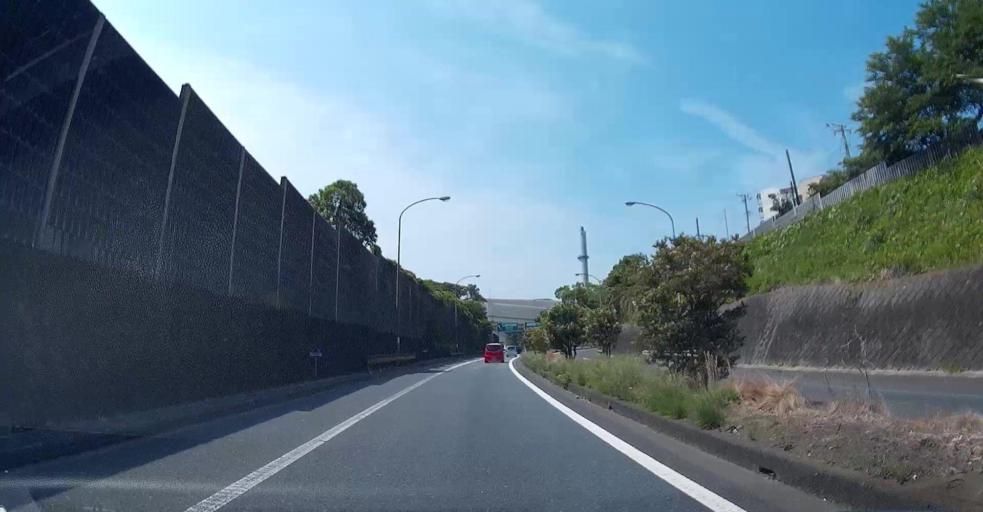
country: JP
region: Kanagawa
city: Yokohama
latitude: 35.4436
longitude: 139.5835
